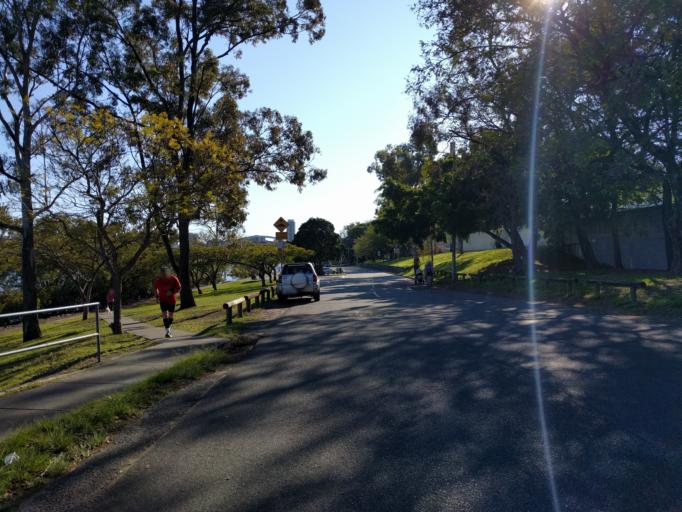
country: AU
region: Queensland
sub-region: Brisbane
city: Milton
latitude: -27.4736
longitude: 153.0086
